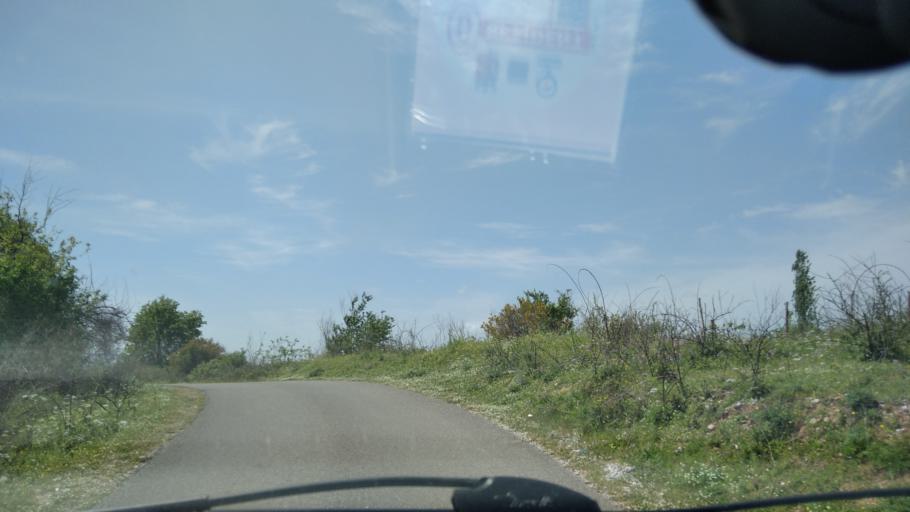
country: AL
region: Shkoder
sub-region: Rrethi i Malesia e Madhe
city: Gruemire
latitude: 42.1478
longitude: 19.5328
